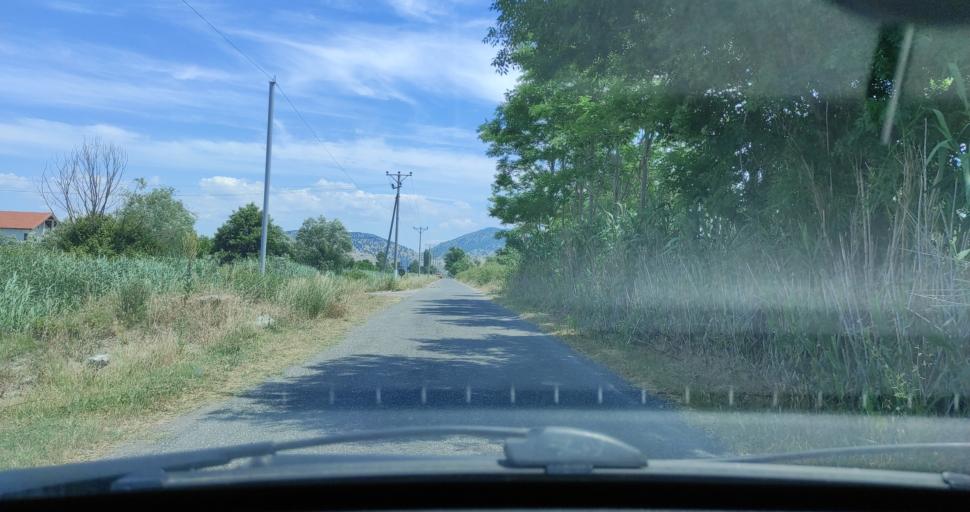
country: AL
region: Shkoder
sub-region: Rrethi i Shkodres
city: Velipoje
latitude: 41.8788
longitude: 19.3934
